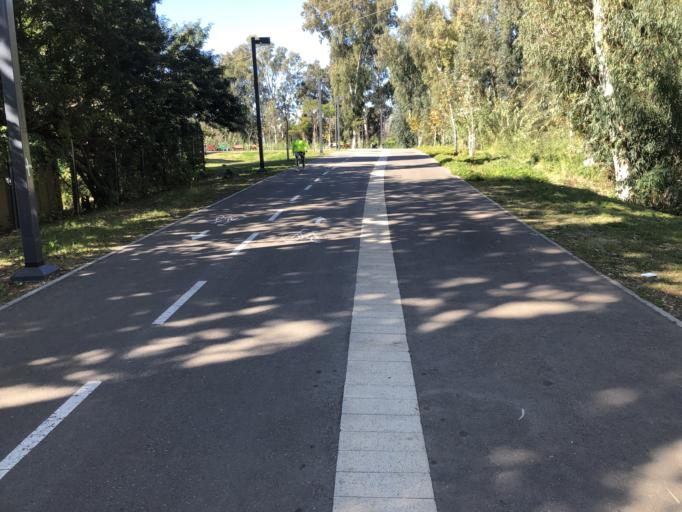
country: IL
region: Tel Aviv
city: Ramat Gan
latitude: 32.0978
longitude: 34.8168
